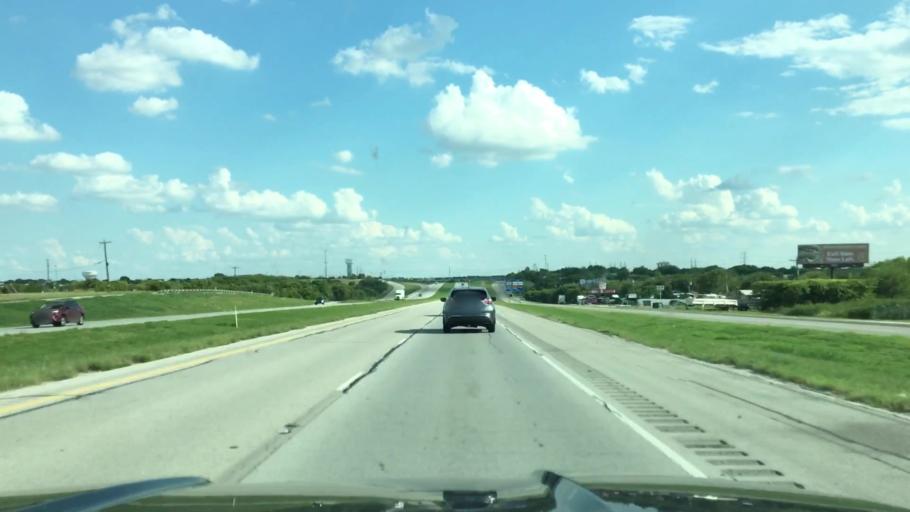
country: US
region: Texas
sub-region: Tarrant County
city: Pecan Acres
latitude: 32.9825
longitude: -97.4266
